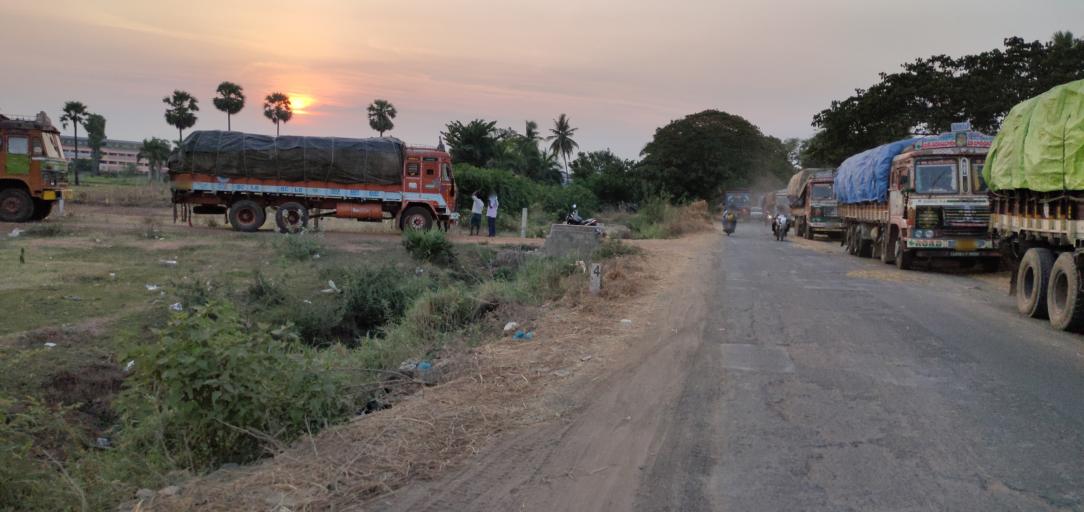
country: IN
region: Andhra Pradesh
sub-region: West Godavari
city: Tadepallegudem
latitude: 16.8464
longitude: 81.4914
